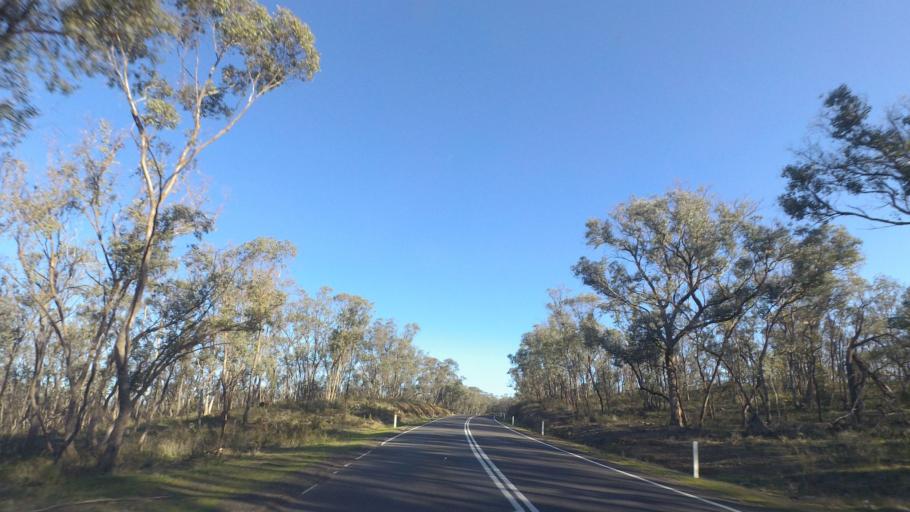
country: AU
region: Victoria
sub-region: Greater Bendigo
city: Kennington
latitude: -36.9219
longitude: 144.4909
